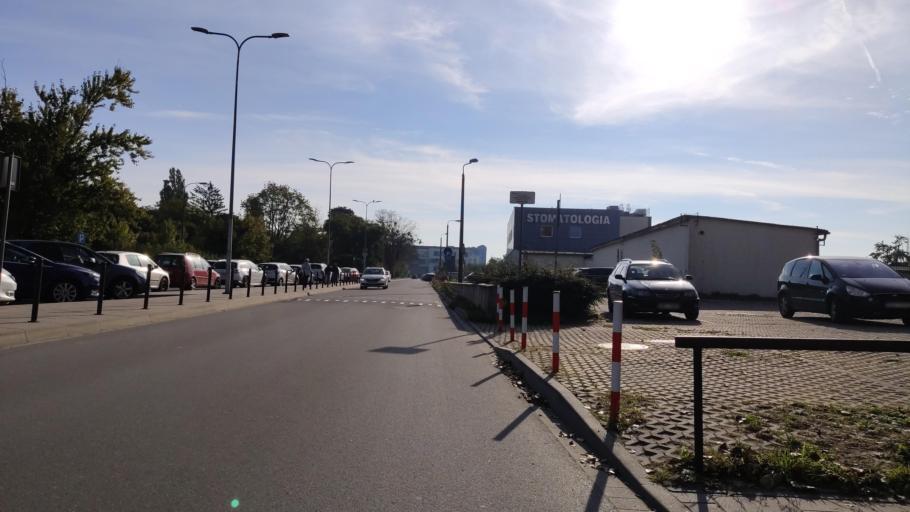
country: PL
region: Lower Silesian Voivodeship
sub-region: Powiat wroclawski
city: Wroclaw
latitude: 51.0758
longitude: 17.0222
